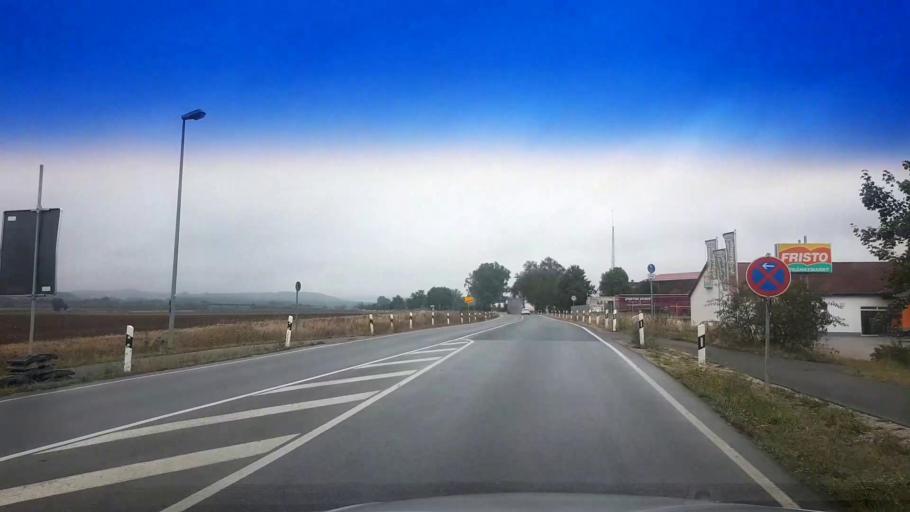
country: DE
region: Bavaria
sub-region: Upper Franconia
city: Eggolsheim
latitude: 49.7703
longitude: 11.0361
